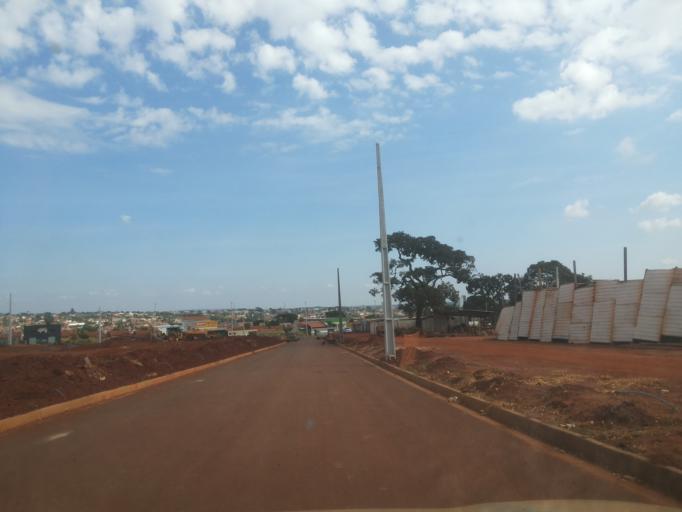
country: BR
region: Minas Gerais
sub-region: Ituiutaba
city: Ituiutaba
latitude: -18.9759
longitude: -49.4387
